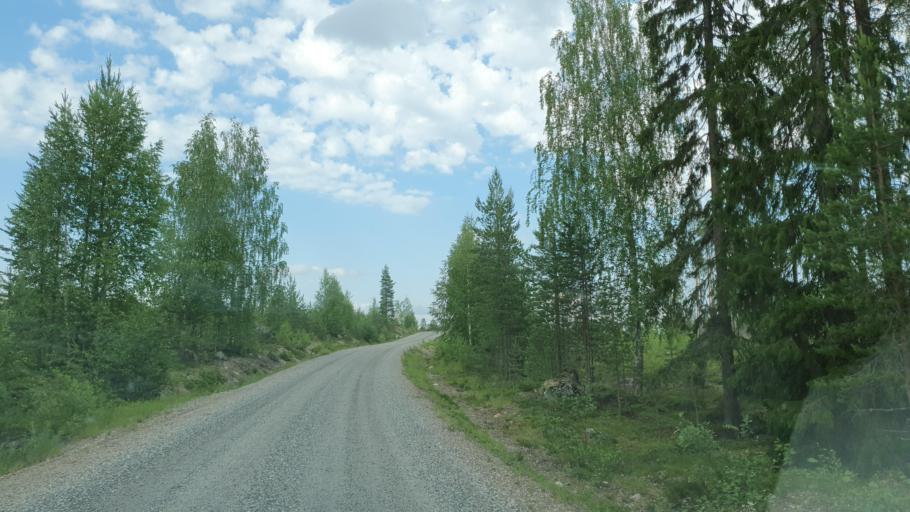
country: FI
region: Kainuu
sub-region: Kehys-Kainuu
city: Kuhmo
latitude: 64.0411
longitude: 29.8238
